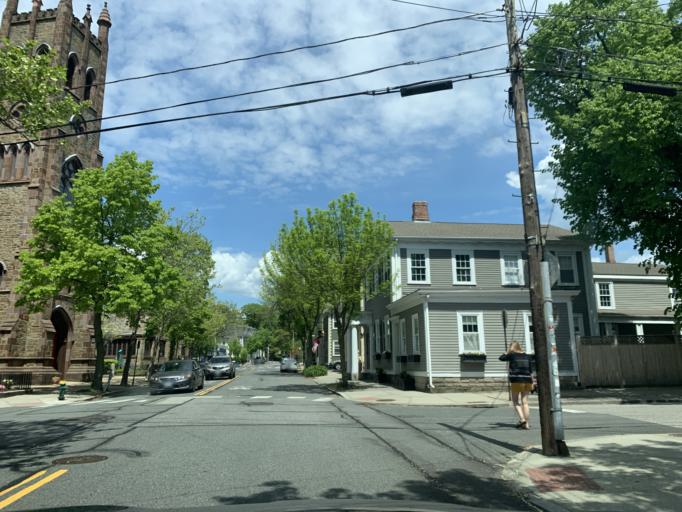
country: US
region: Rhode Island
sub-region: Providence County
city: Providence
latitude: 41.8211
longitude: -71.3961
